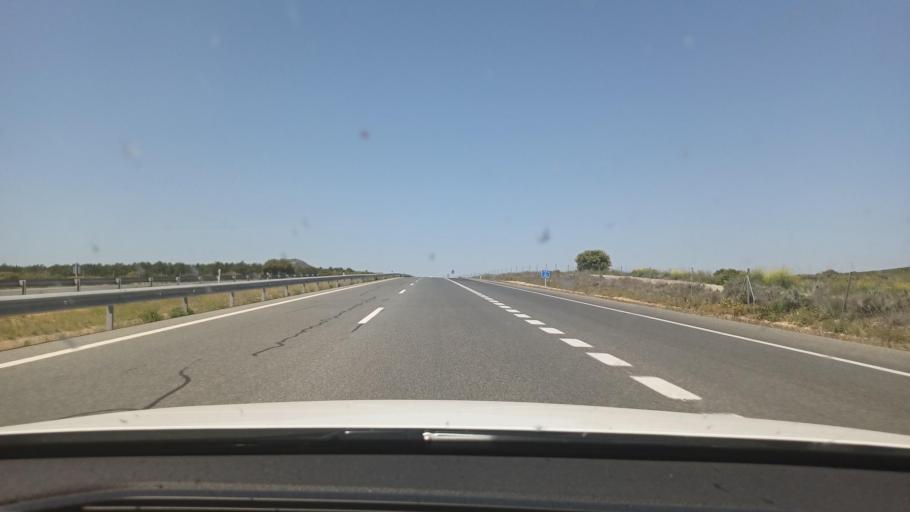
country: ES
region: Castille-La Mancha
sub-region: Provincia de Albacete
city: Higueruela
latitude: 38.8969
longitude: -1.4329
